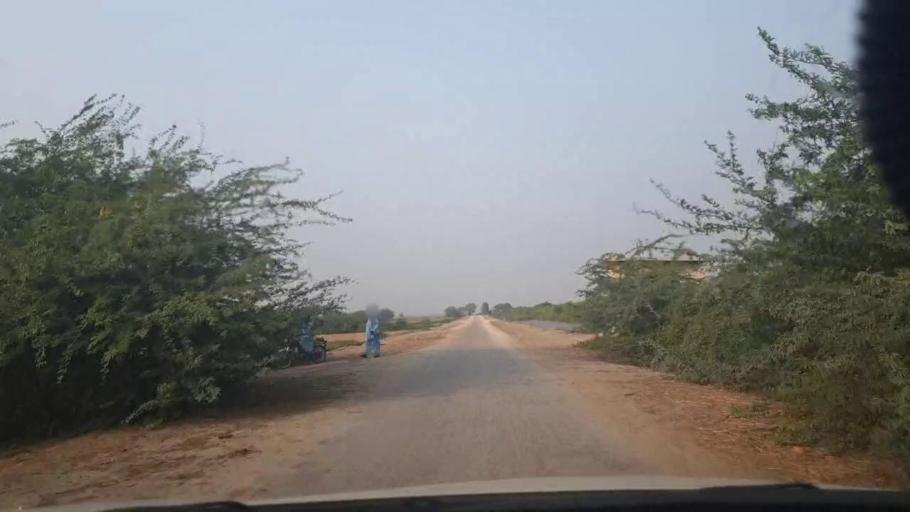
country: PK
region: Sindh
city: Bulri
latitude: 24.8335
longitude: 68.4029
